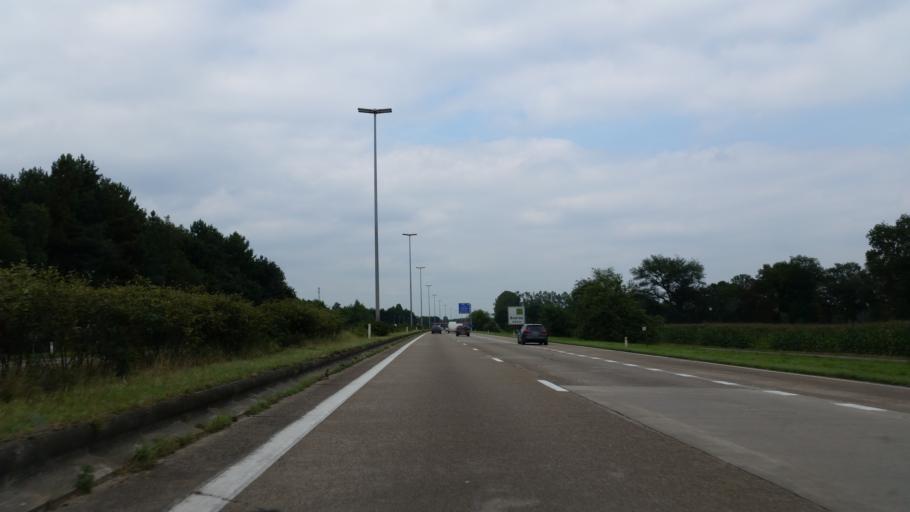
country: BE
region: Flanders
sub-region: Provincie Antwerpen
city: Beerse
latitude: 51.2813
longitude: 4.8470
